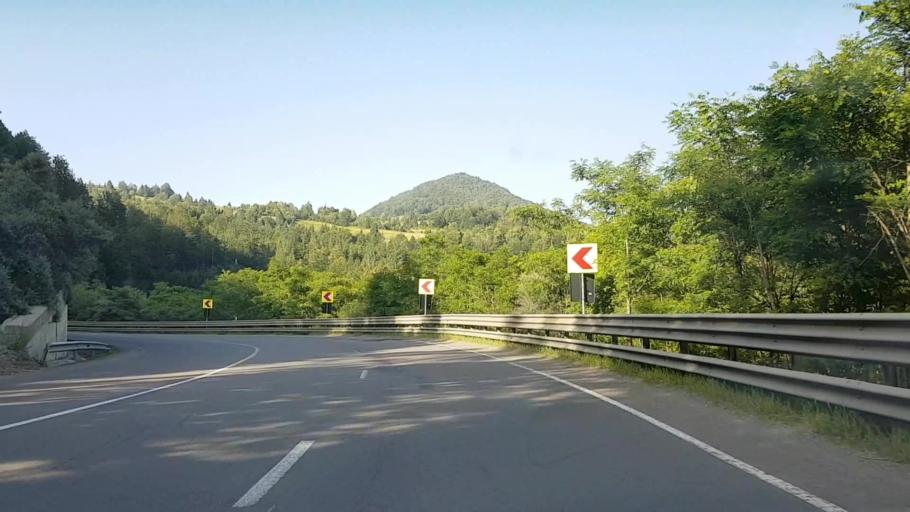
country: RO
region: Bistrita-Nasaud
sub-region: Comuna Tiha Bargaului
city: Tureac
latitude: 47.2223
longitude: 24.9122
